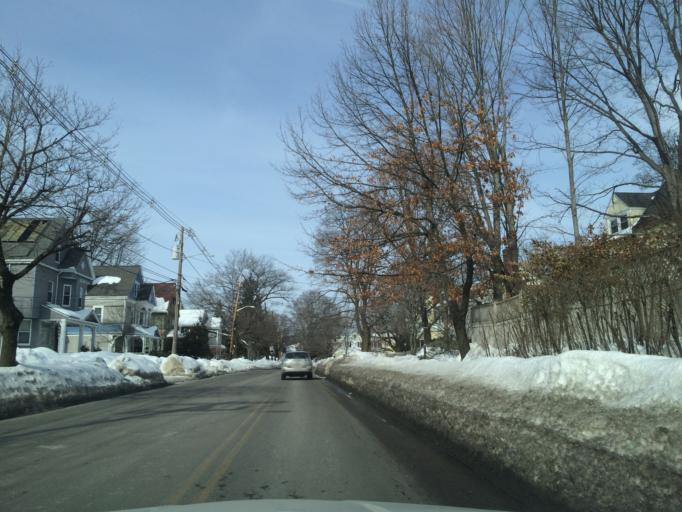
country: US
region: Massachusetts
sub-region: Middlesex County
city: Waltham
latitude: 42.3487
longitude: -71.2472
